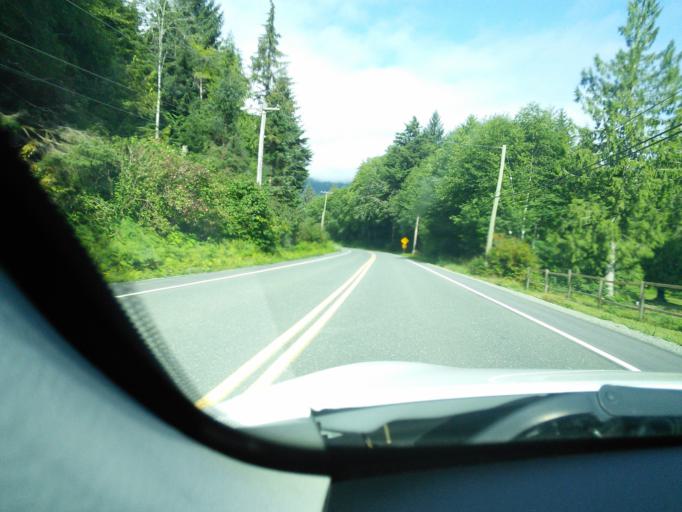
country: CA
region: British Columbia
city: Campbell River
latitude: 50.3625
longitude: -125.9285
